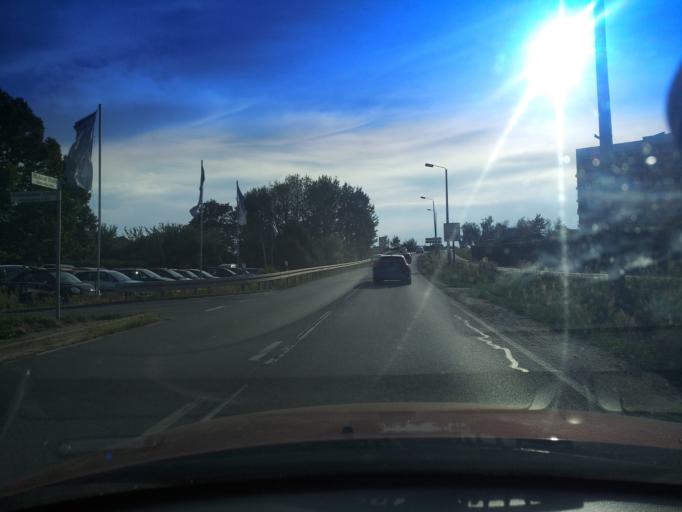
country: DE
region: Saxony
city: Bautzen
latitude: 51.1885
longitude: 14.4487
